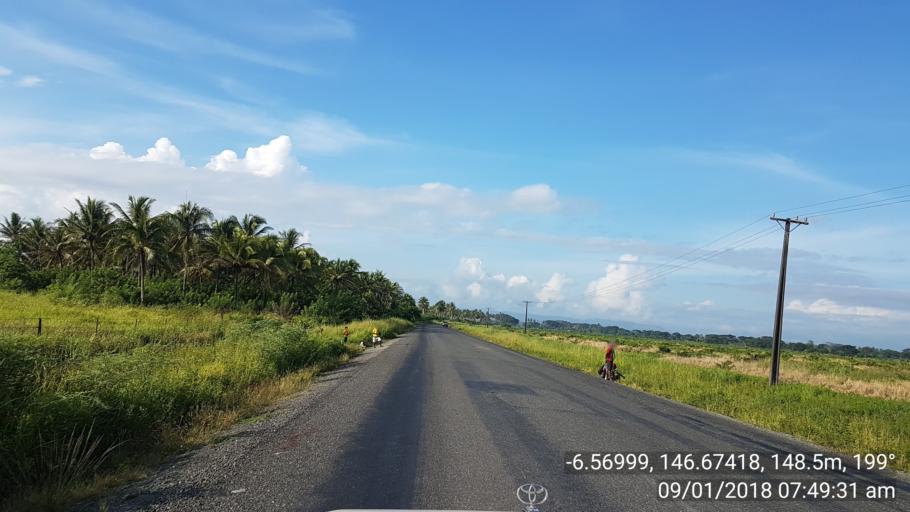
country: PG
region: Morobe
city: Lae
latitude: -6.5698
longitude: 146.6743
